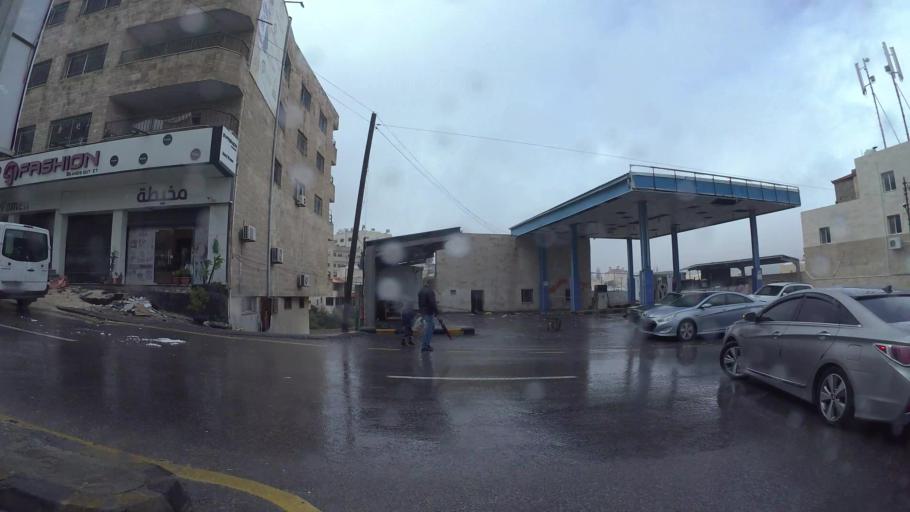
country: JO
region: Amman
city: Wadi as Sir
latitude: 32.0052
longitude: 35.7866
